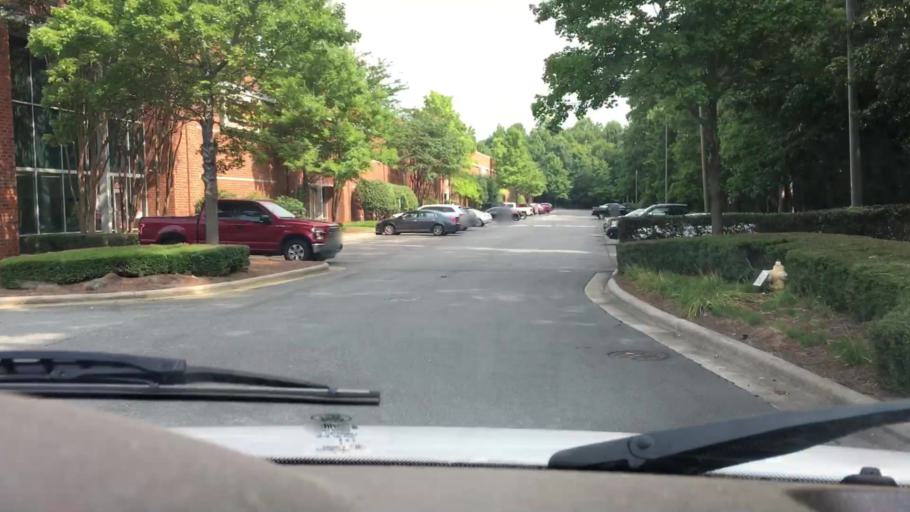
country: US
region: North Carolina
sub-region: Mecklenburg County
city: Charlotte
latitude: 35.3169
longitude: -80.8484
